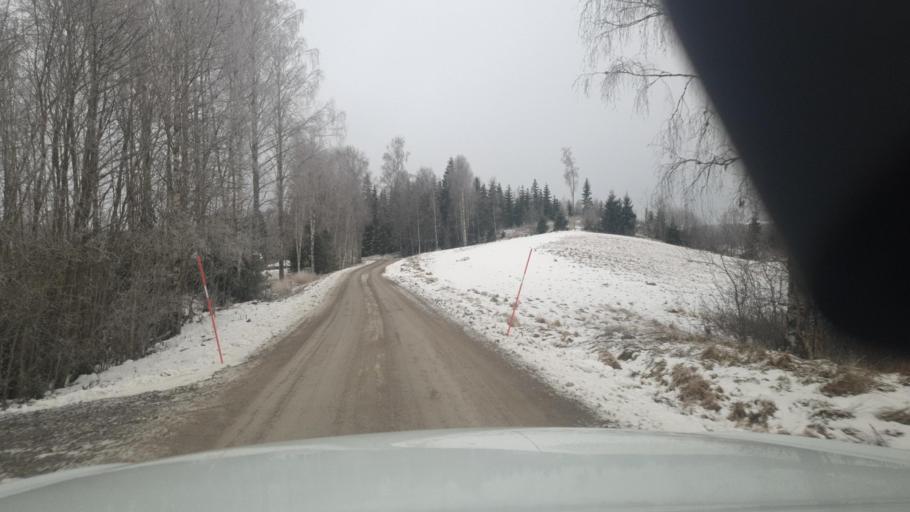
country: SE
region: Vaermland
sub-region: Torsby Kommun
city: Torsby
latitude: 59.9369
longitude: 12.8162
